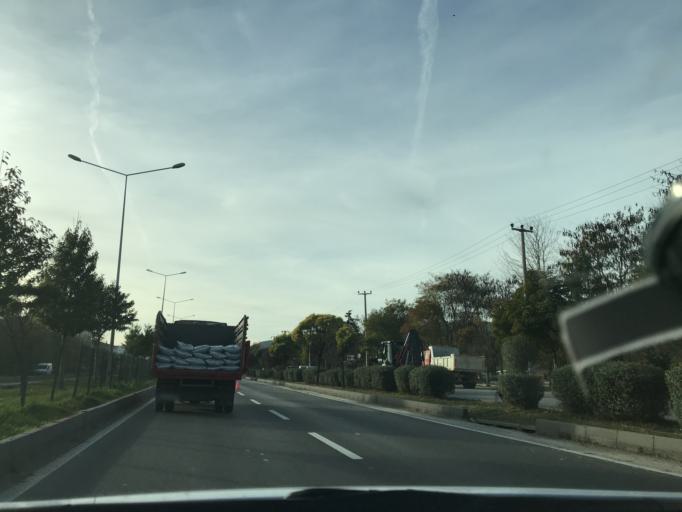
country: TR
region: Bolu
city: Bolu
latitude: 40.7382
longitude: 31.6152
